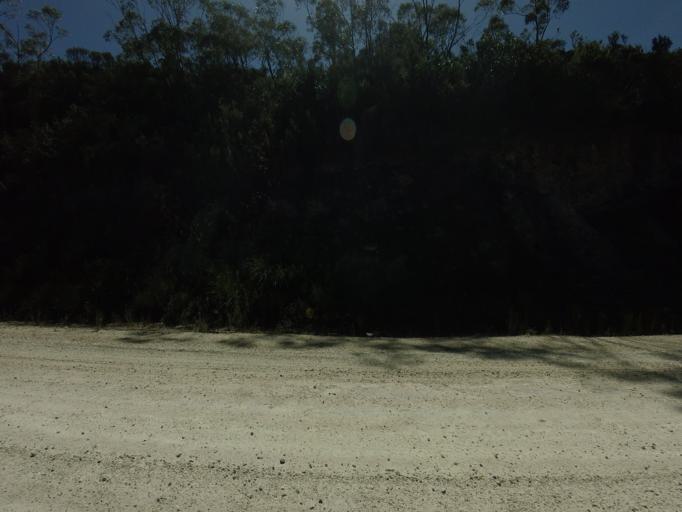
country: AU
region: Tasmania
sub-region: Huon Valley
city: Geeveston
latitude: -42.9324
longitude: 146.3430
